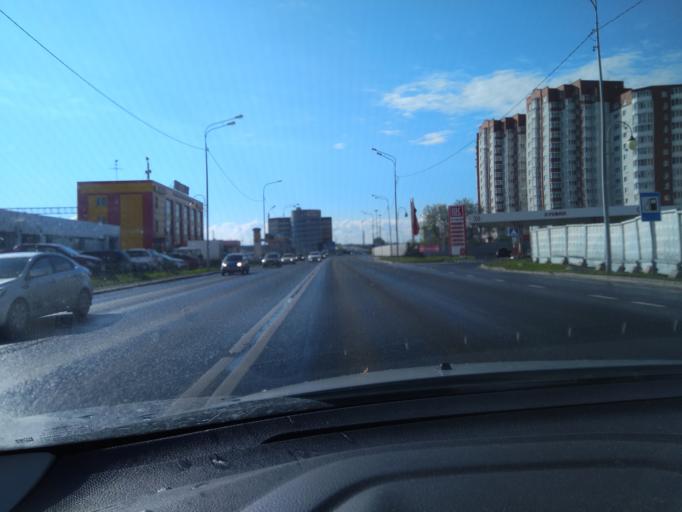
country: RU
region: Tjumen
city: Tyumen
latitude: 57.1395
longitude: 65.5441
